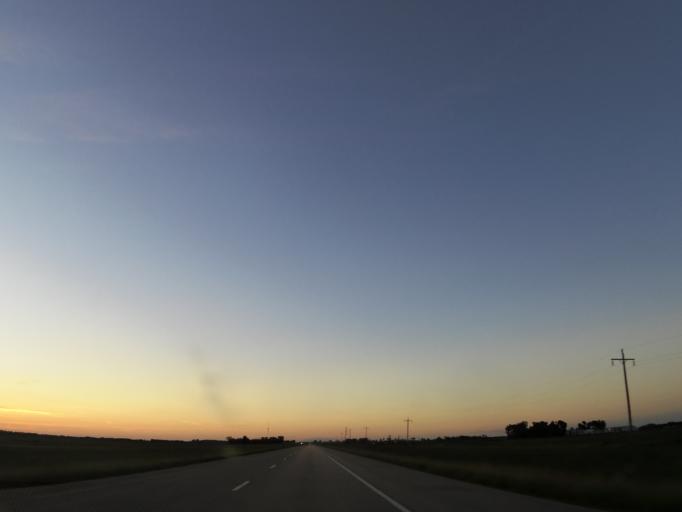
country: US
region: North Dakota
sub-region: Grand Forks County
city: Grand Forks
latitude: 48.1744
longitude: -97.1888
